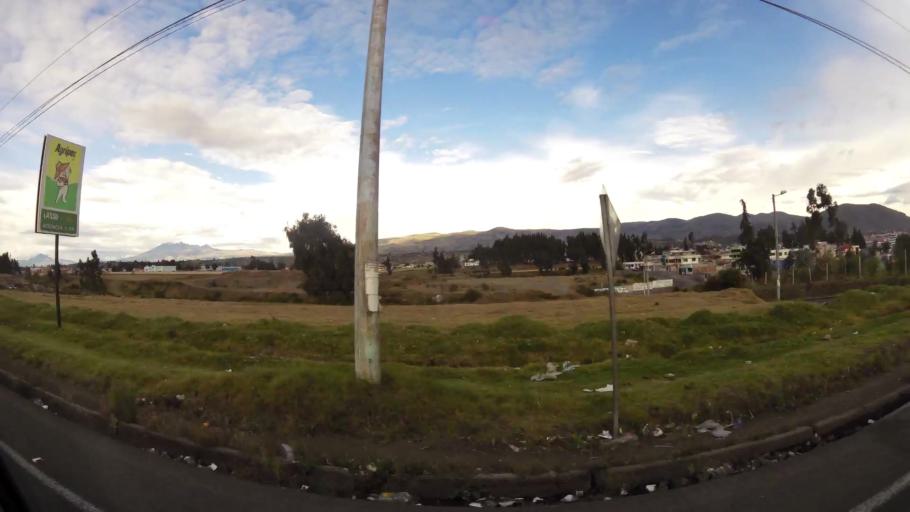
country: EC
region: Cotopaxi
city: Latacunga
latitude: -0.9172
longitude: -78.6276
